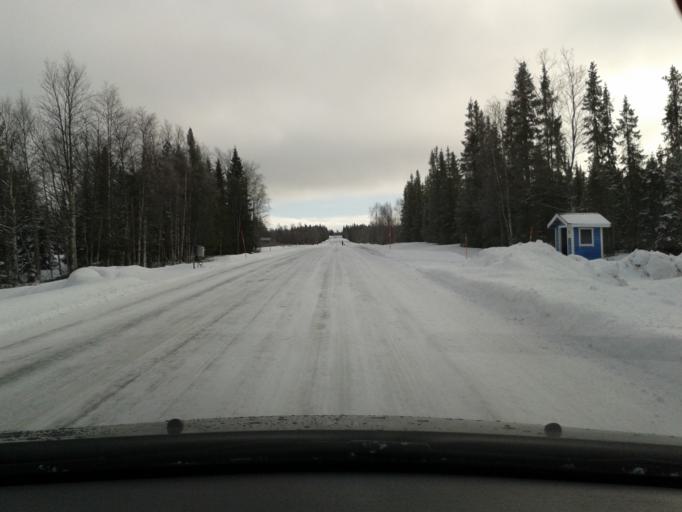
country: SE
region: Vaesterbotten
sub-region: Vilhelmina Kommun
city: Sjoberg
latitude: 64.7879
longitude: 16.1014
